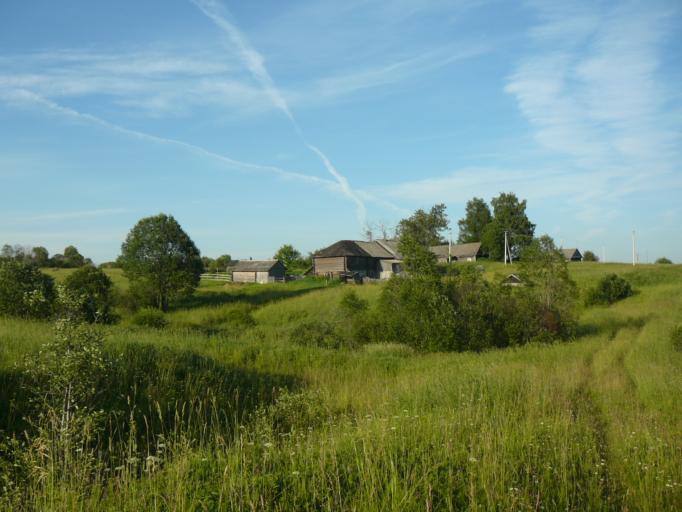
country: RU
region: Vologda
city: Ust'ye
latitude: 60.1433
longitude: 39.6035
